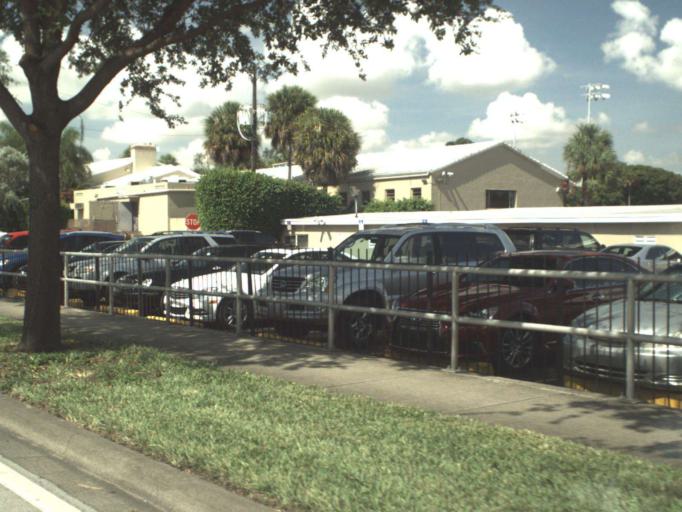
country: US
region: Florida
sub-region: Miami-Dade County
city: Biscayne Park
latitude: 25.8687
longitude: -80.1754
